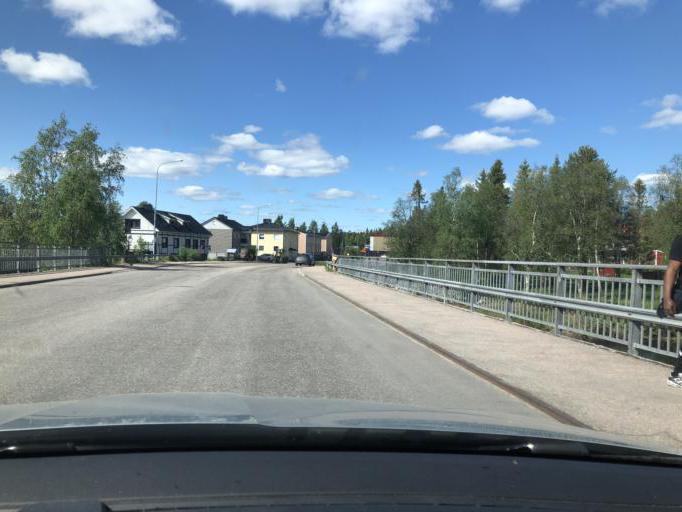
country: SE
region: Norrbotten
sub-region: Gallivare Kommun
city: Gaellivare
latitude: 67.1319
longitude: 20.6828
